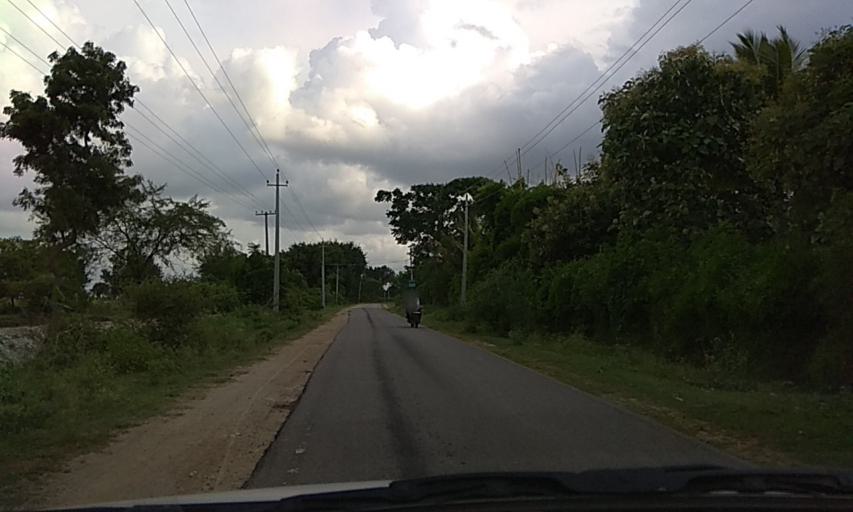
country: IN
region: Karnataka
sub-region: Chamrajnagar
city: Gundlupet
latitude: 11.8770
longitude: 76.7472
